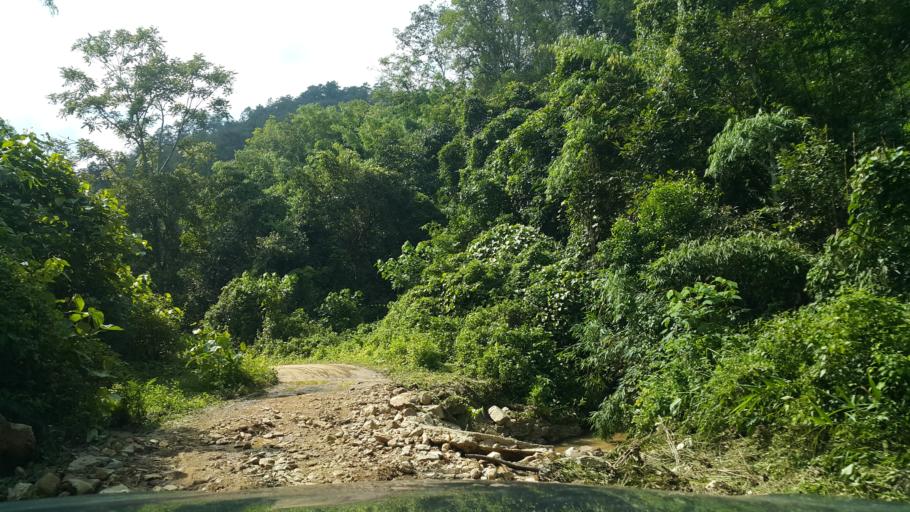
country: TH
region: Chiang Mai
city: Phrao
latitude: 19.0919
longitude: 99.2604
